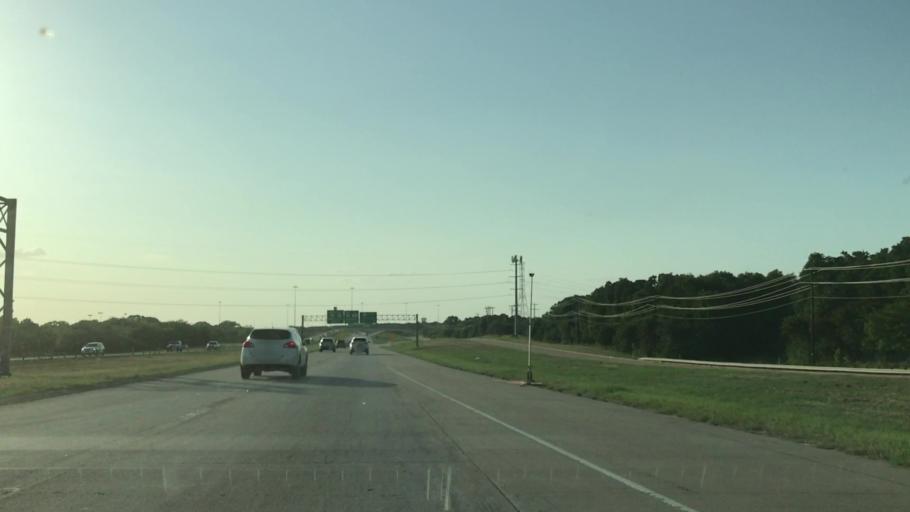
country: US
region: Texas
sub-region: Tarrant County
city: Grapevine
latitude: 32.8973
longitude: -97.0889
